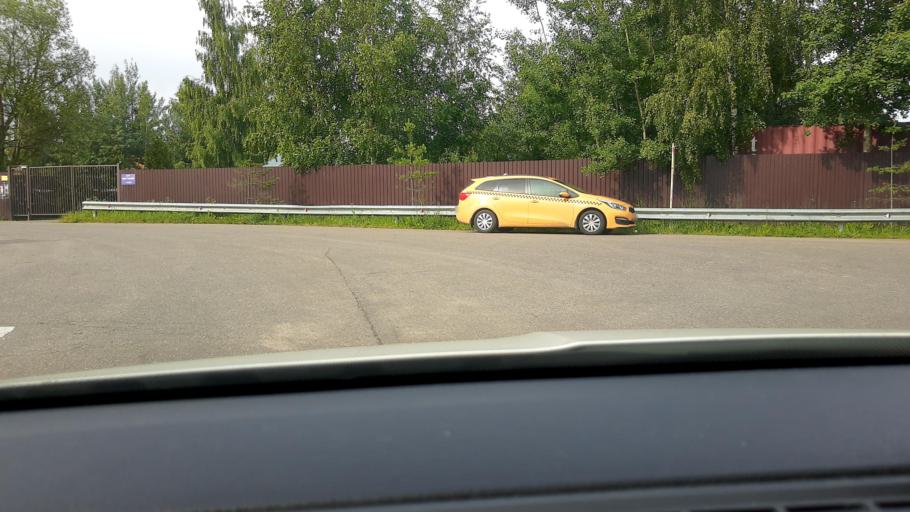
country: RU
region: Moskovskaya
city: Troitsk
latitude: 55.4917
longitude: 37.2600
